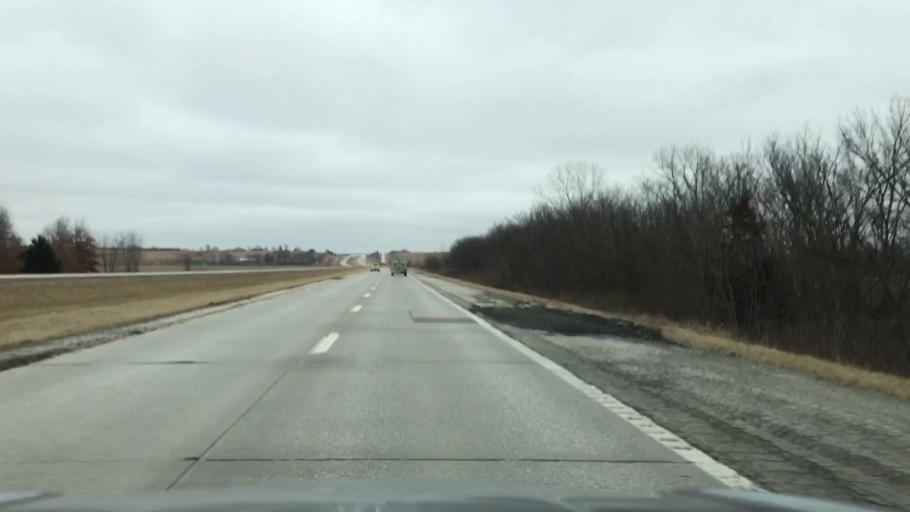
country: US
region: Missouri
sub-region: Linn County
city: Marceline
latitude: 39.7611
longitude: -92.9736
